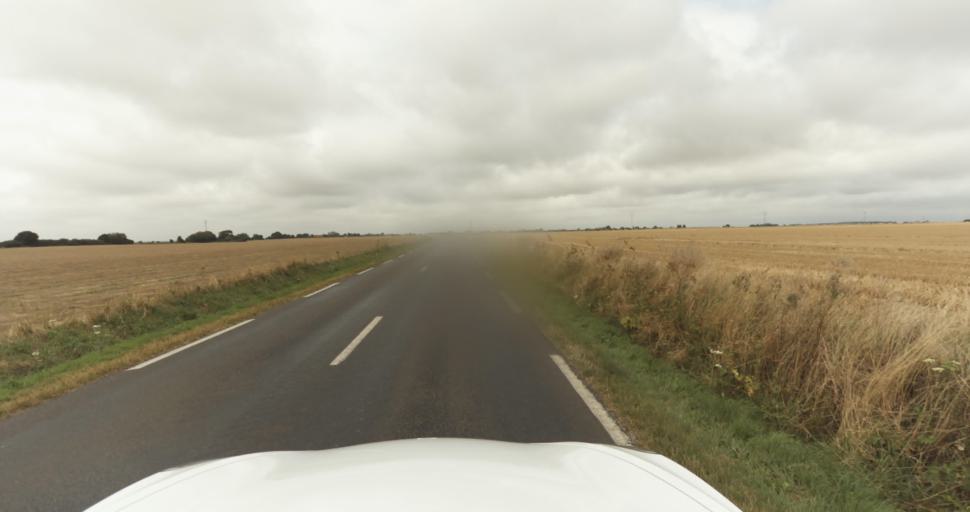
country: FR
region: Haute-Normandie
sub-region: Departement de l'Eure
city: Claville
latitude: 49.0783
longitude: 1.0587
